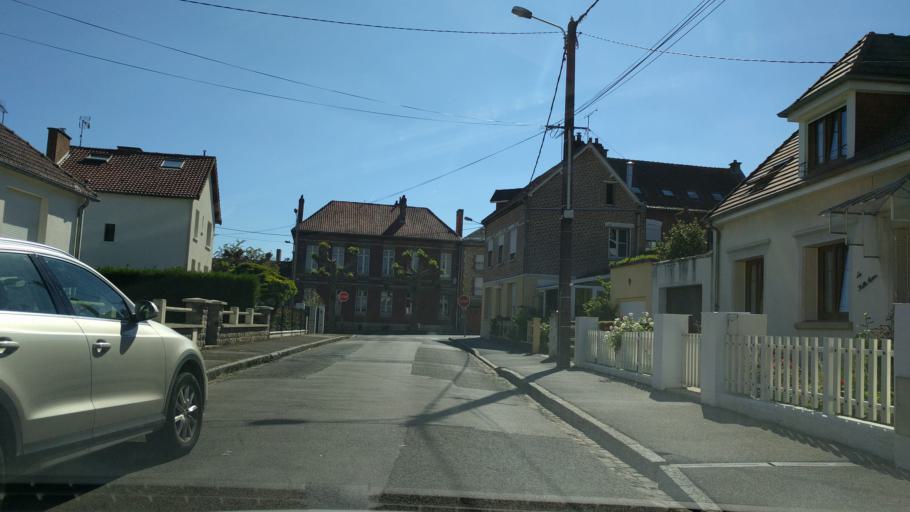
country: FR
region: Picardie
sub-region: Departement de la Somme
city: Peronne
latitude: 49.9301
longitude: 2.9382
